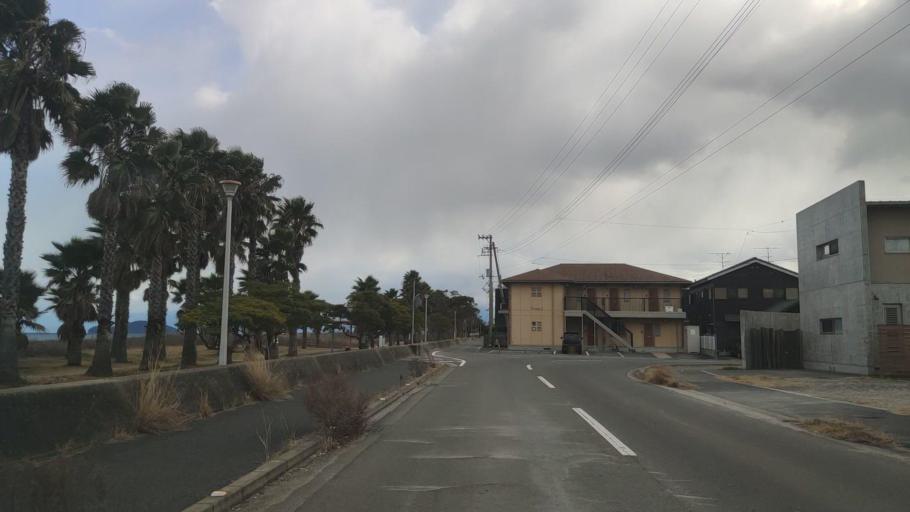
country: JP
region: Ehime
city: Saijo
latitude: 34.0451
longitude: 133.0293
